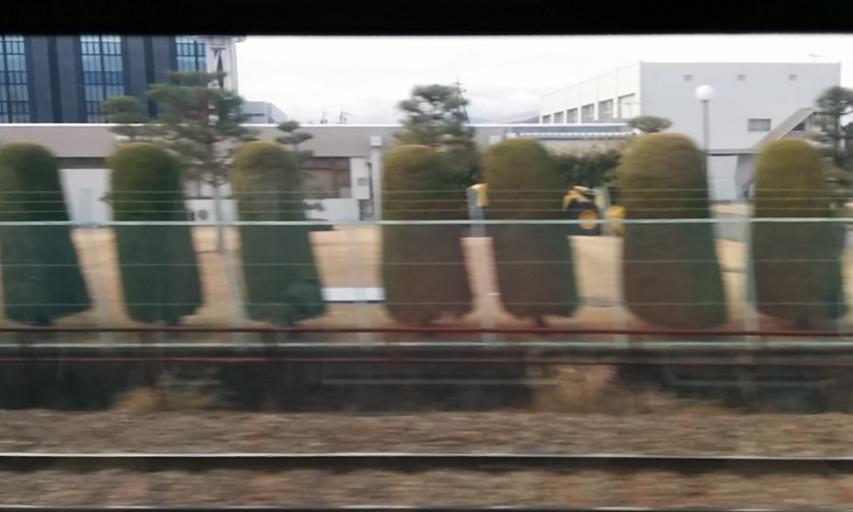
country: JP
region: Nagano
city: Matsumoto
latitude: 36.2034
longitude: 137.9669
